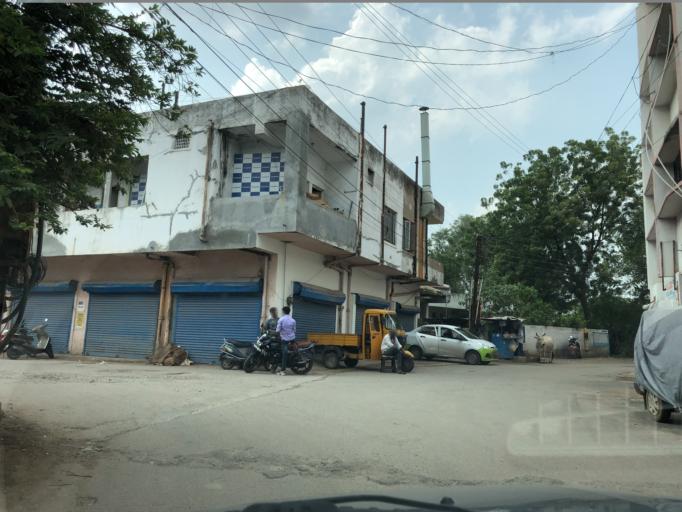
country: IN
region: Telangana
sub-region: Hyderabad
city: Malkajgiri
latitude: 17.4465
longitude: 78.4799
